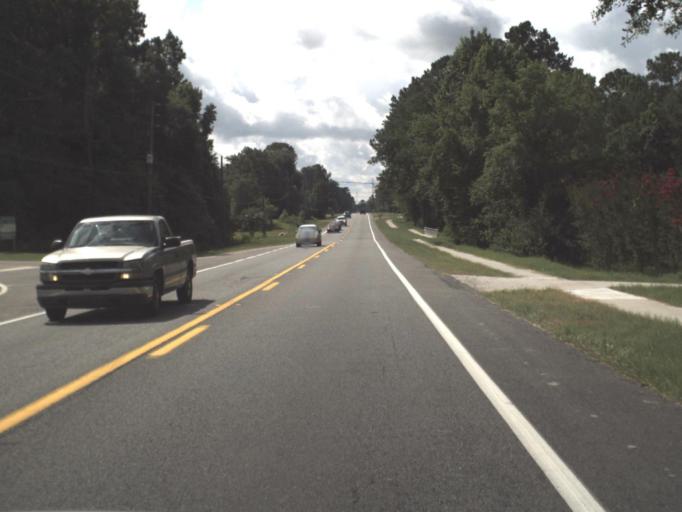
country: US
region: Florida
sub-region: Baker County
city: Macclenny
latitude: 30.2718
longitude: -82.1186
